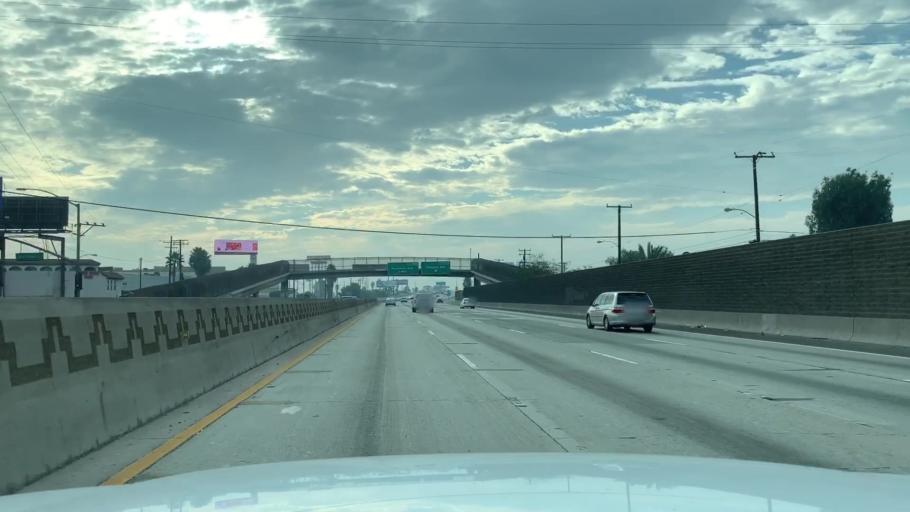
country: US
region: California
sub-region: Los Angeles County
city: Bell Gardens
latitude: 33.9800
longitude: -118.1291
